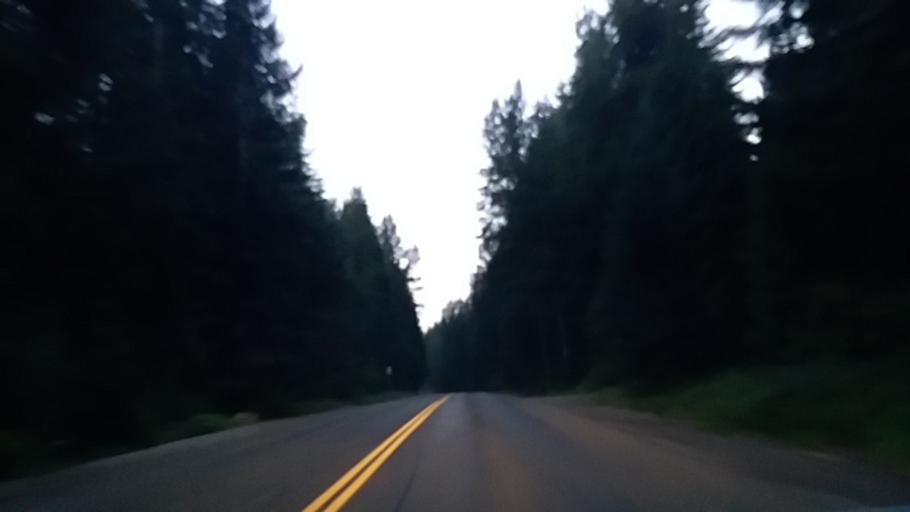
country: US
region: Washington
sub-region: Kittitas County
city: Cle Elum
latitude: 47.3278
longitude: -121.2670
